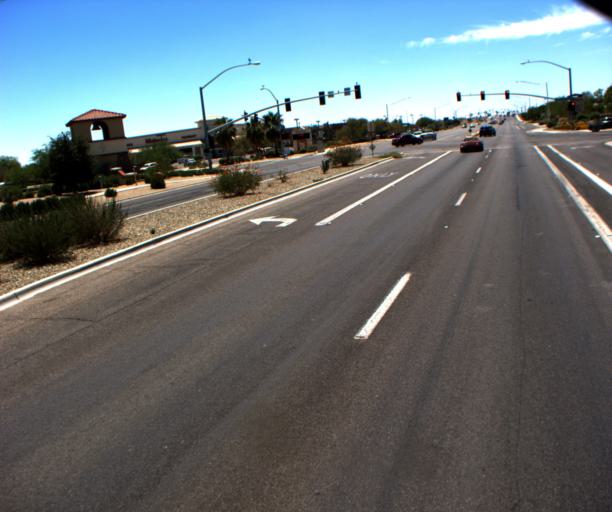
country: US
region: Arizona
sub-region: Pinal County
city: Casa Grande
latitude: 32.8798
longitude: -111.6785
